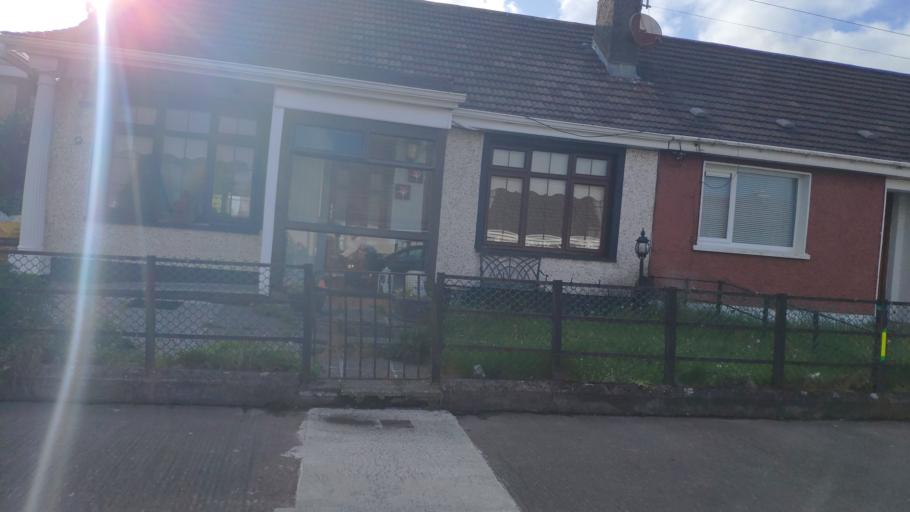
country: IE
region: Munster
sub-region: County Cork
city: Cork
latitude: 51.9113
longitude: -8.4828
